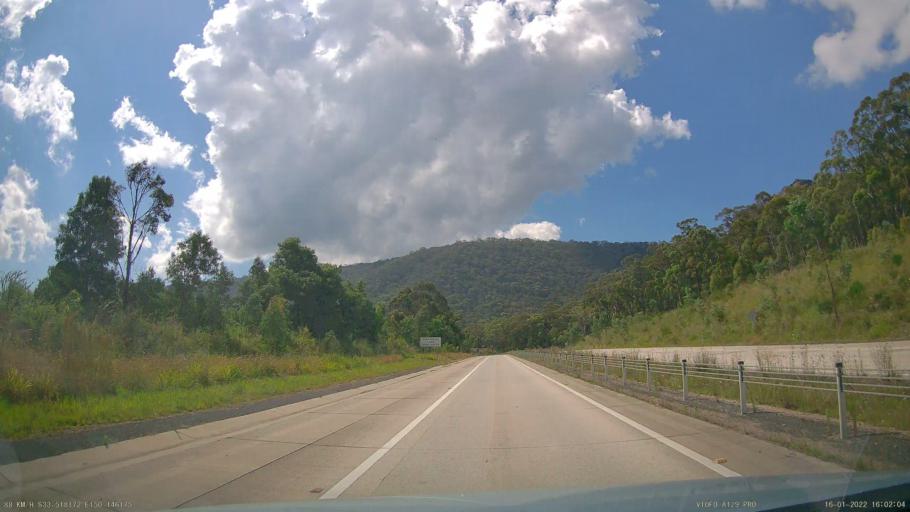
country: AU
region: New South Wales
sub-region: Lithgow
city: Bowenfels
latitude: -33.5179
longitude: 150.1459
